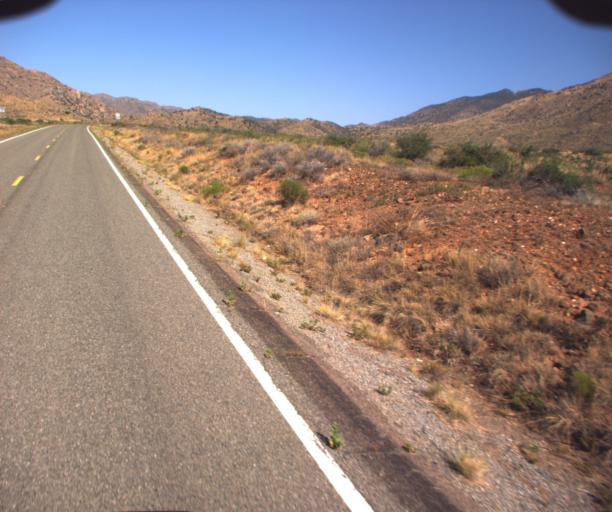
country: US
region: Arizona
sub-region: Graham County
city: Swift Trail Junction
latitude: 32.5604
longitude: -109.7686
